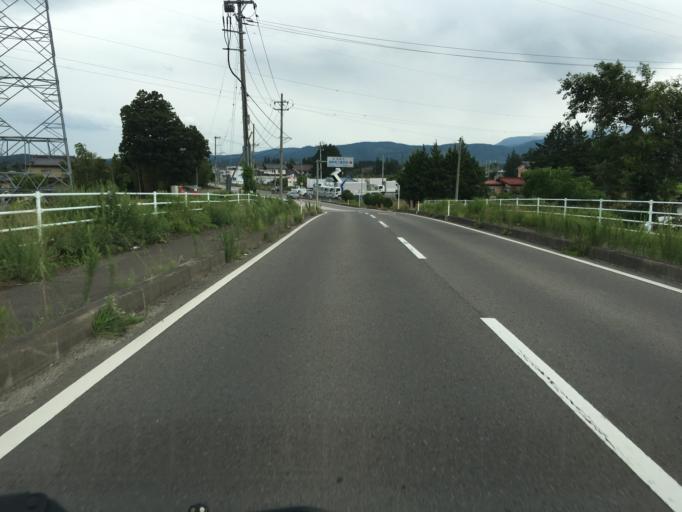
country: JP
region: Fukushima
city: Fukushima-shi
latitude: 37.7552
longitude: 140.4016
